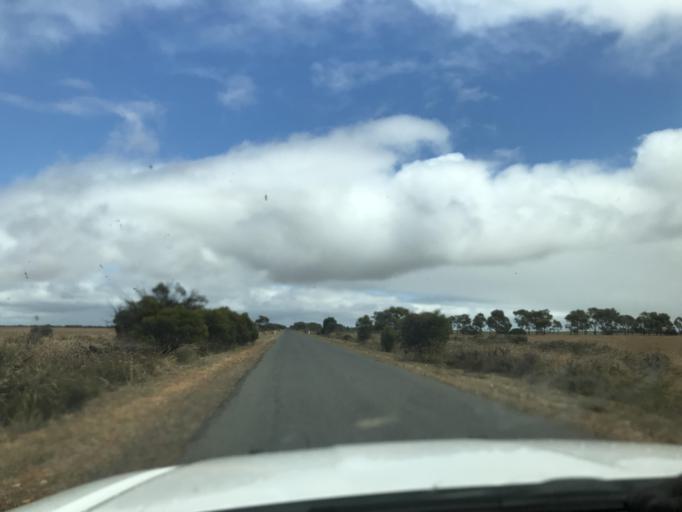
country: AU
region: South Australia
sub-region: Tatiara
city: Bordertown
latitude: -36.1380
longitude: 141.2067
